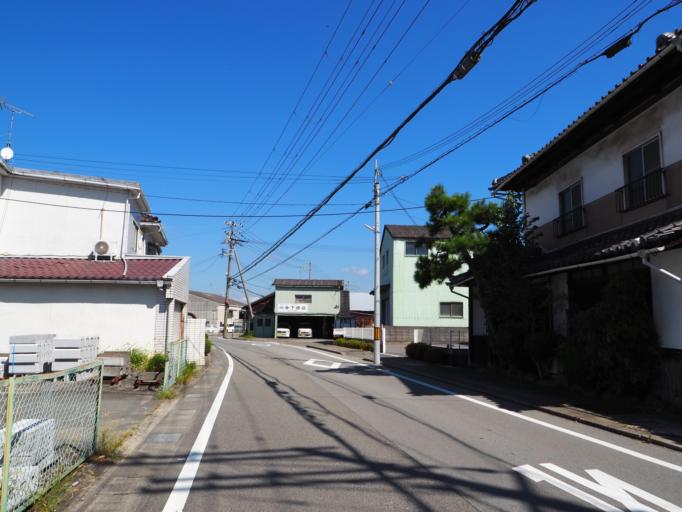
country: JP
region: Hyogo
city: Tatsunocho-tominaga
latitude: 34.7844
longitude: 134.5932
